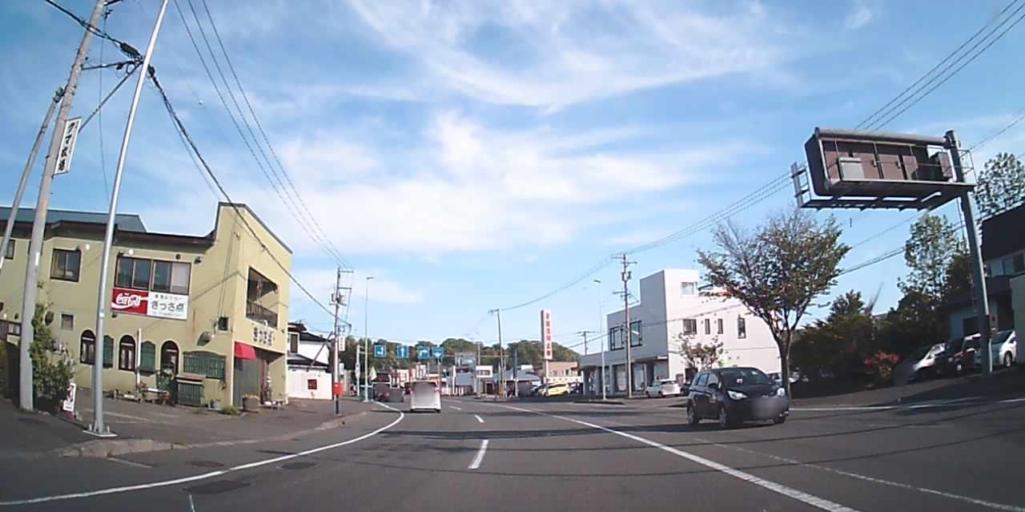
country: JP
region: Hokkaido
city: Shiraoi
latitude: 42.4554
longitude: 141.1772
